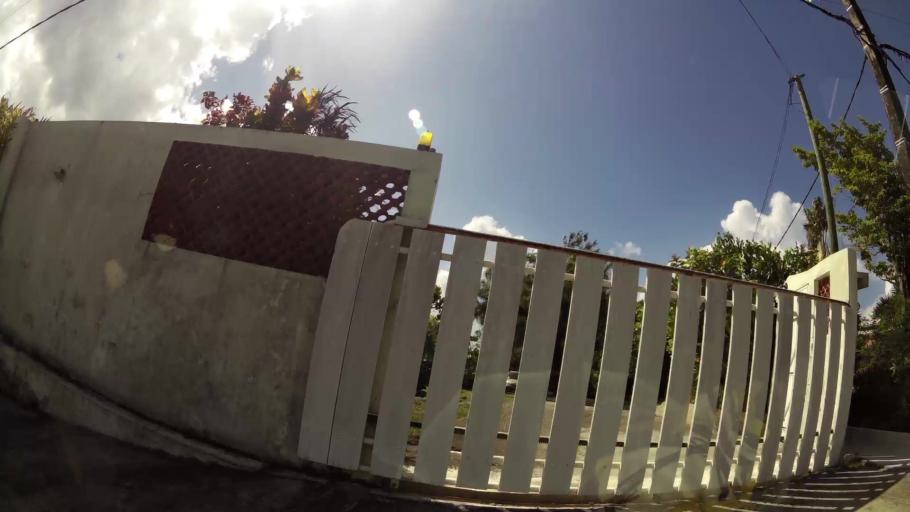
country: MQ
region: Martinique
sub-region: Martinique
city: Fort-de-France
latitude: 14.6324
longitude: -61.1230
